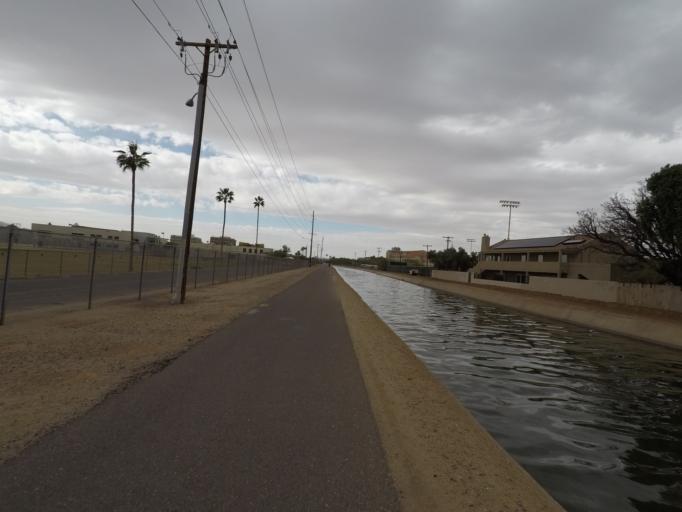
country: US
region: Arizona
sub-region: Maricopa County
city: Phoenix
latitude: 33.5033
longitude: -112.0687
